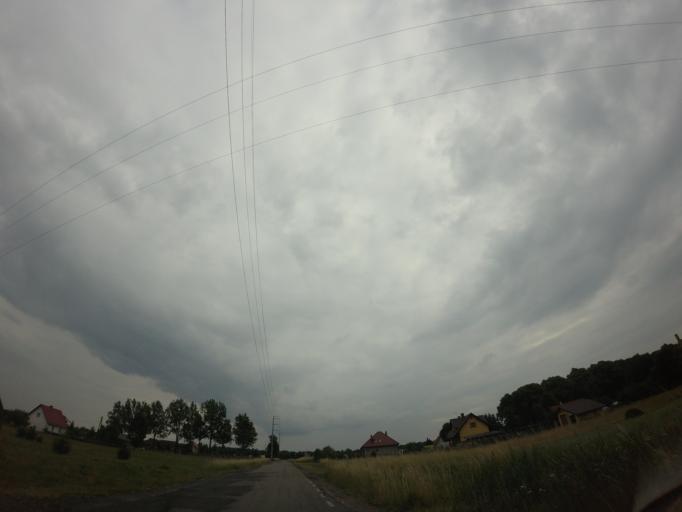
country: PL
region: West Pomeranian Voivodeship
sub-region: Powiat drawski
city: Czaplinek
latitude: 53.5171
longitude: 16.2254
